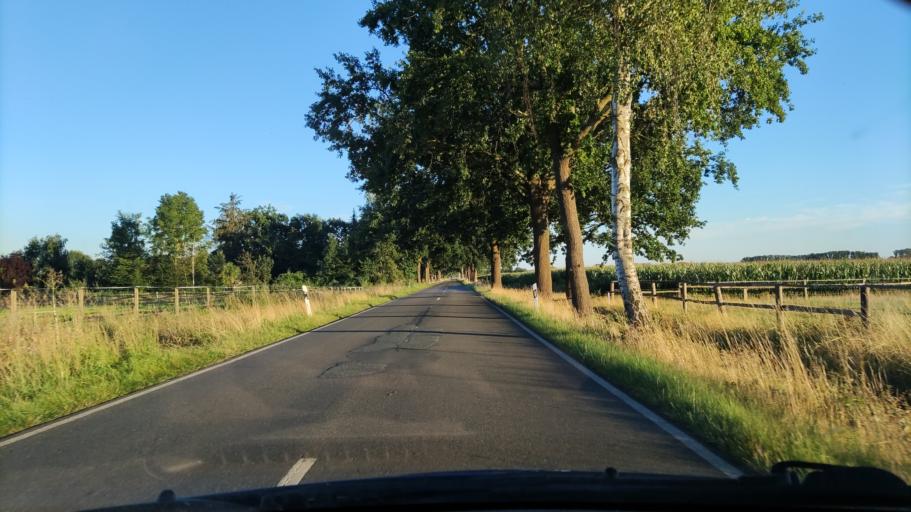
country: DE
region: Lower Saxony
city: Luechow
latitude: 52.9970
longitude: 11.1530
